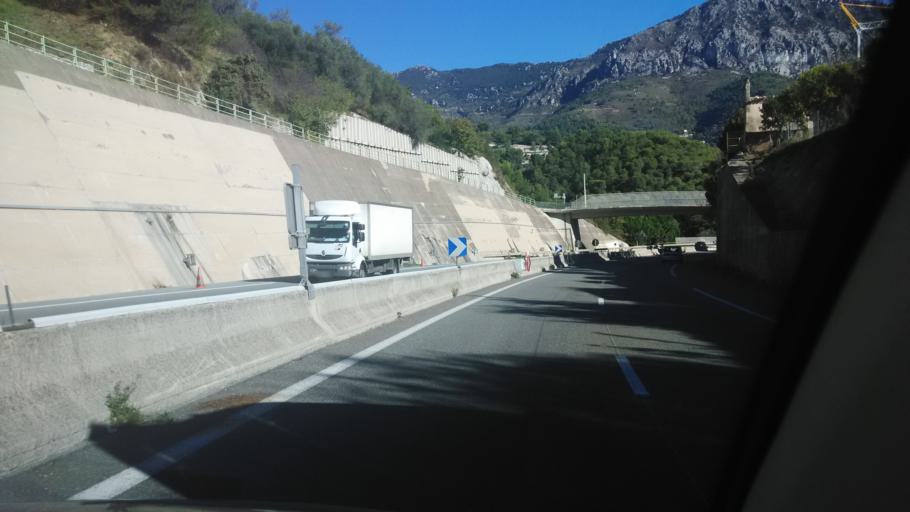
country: FR
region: Provence-Alpes-Cote d'Azur
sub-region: Departement des Alpes-Maritimes
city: Sainte-Agnes
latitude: 43.7951
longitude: 7.4764
